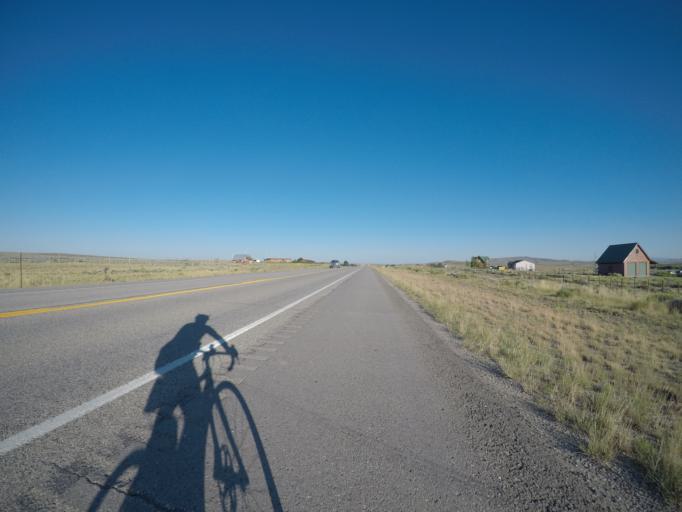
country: US
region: Wyoming
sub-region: Sublette County
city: Pinedale
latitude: 42.8777
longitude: -109.9584
